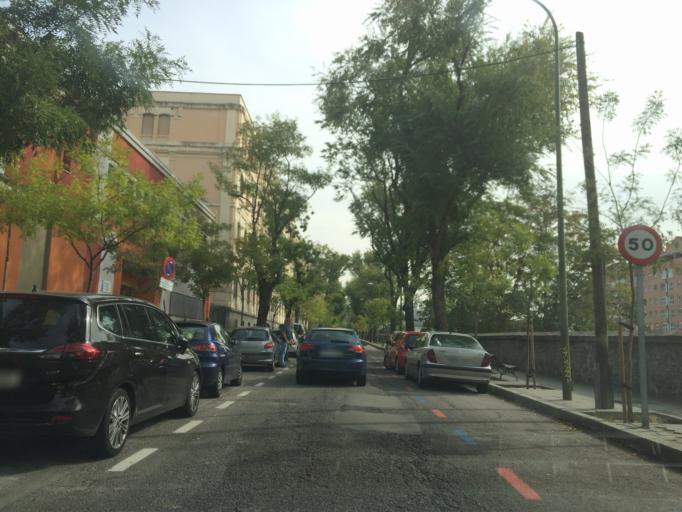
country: ES
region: Madrid
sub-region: Provincia de Madrid
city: Moncloa-Aravaca
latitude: 40.4253
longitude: -3.7230
